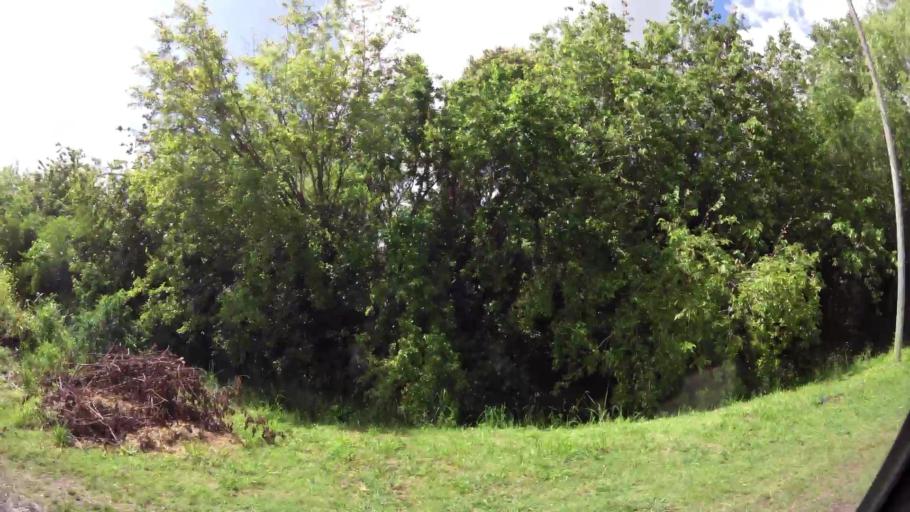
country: AR
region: Buenos Aires
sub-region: Partido de Quilmes
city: Quilmes
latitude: -34.8386
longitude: -58.1768
